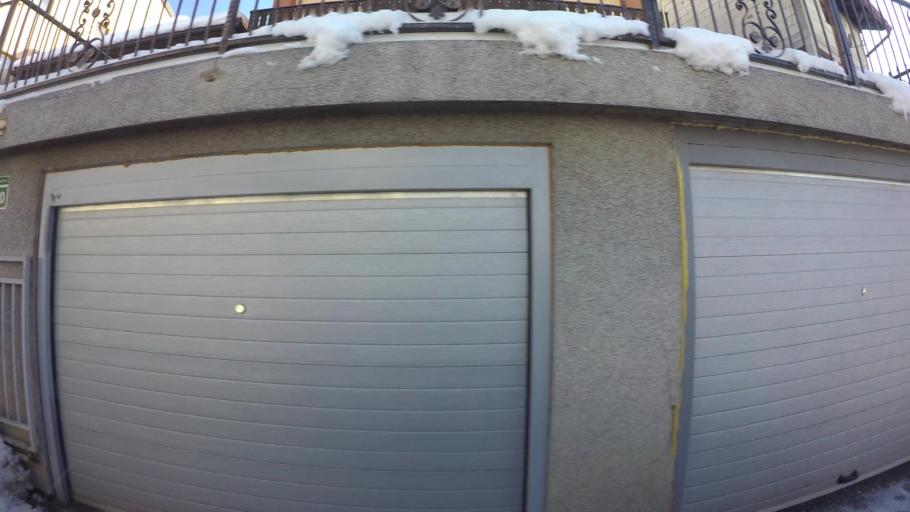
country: BA
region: Federation of Bosnia and Herzegovina
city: Kobilja Glava
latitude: 43.8759
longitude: 18.4224
